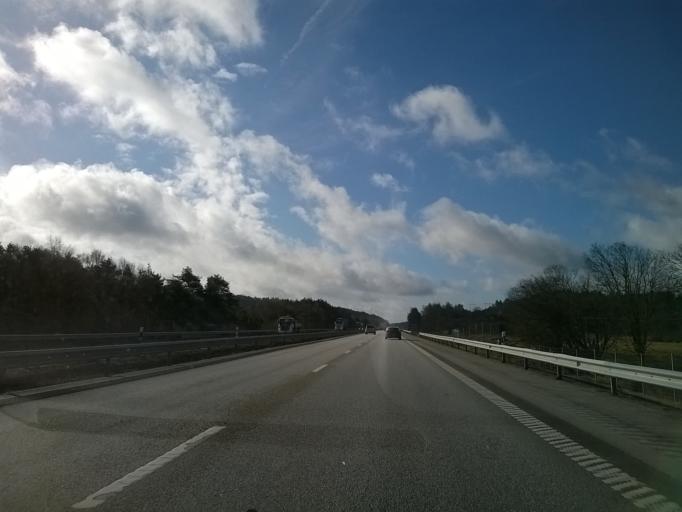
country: SE
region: Vaestra Goetaland
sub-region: Molndal
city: Lindome
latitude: 57.5406
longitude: 12.0519
